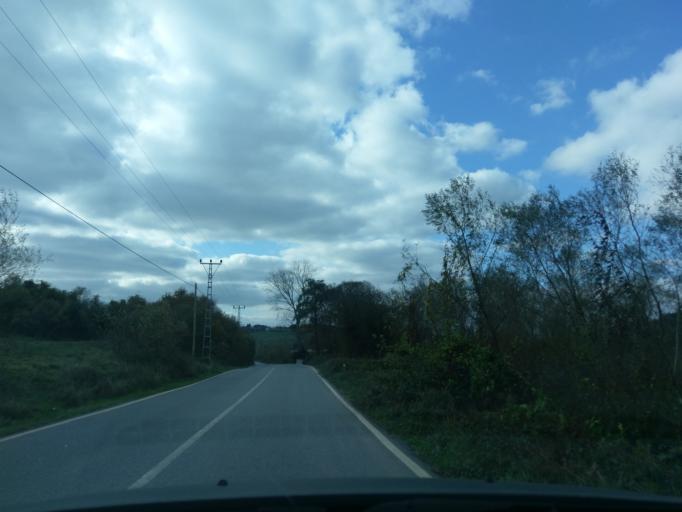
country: TR
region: Istanbul
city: Durusu
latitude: 41.3144
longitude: 28.7038
